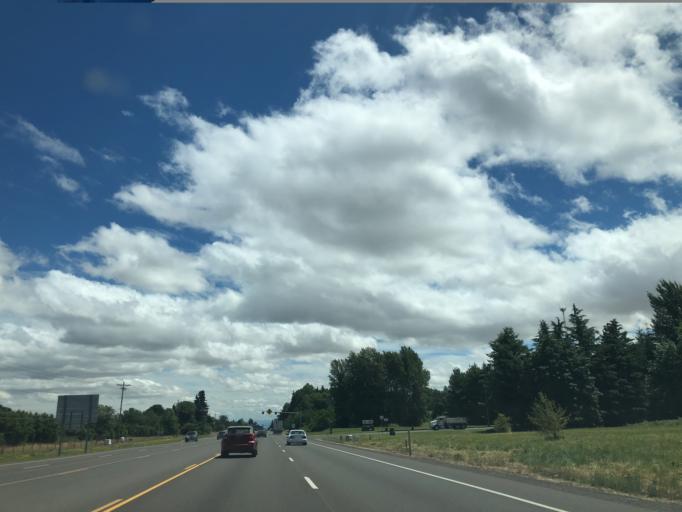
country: US
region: Oregon
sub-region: Benton County
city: Corvallis
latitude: 44.5639
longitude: -123.2433
